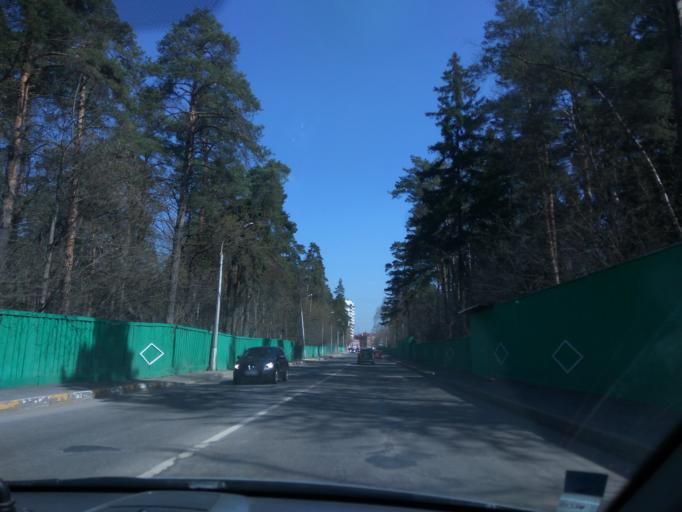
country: RU
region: Moskovskaya
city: Kratovo
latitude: 55.5804
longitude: 38.1944
